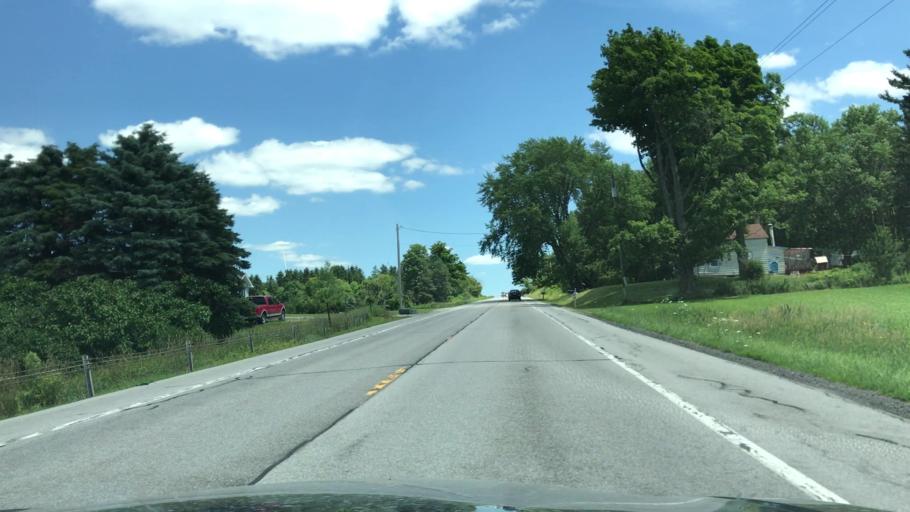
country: US
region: New York
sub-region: Wyoming County
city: Attica
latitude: 42.7522
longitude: -78.2585
